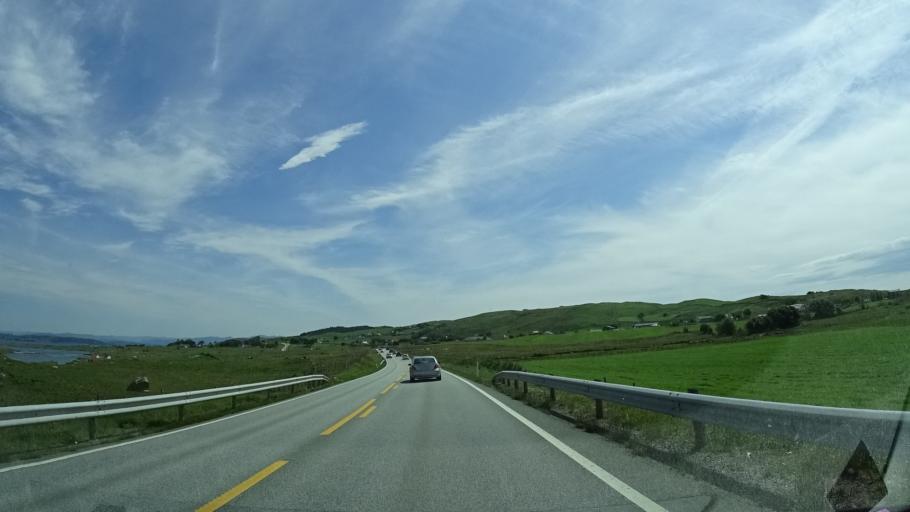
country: NO
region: Rogaland
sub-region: Rennesoy
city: Vikevag
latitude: 59.1293
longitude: 5.6146
